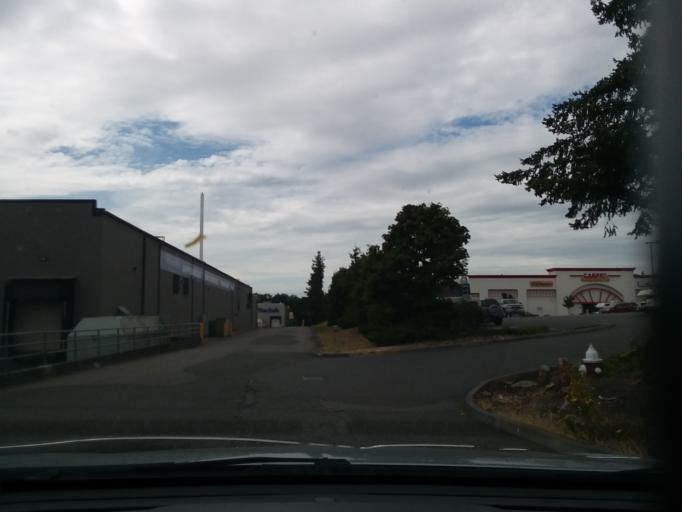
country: US
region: Washington
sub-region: Whatcom County
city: Bellingham
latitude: 48.7861
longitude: -122.4818
